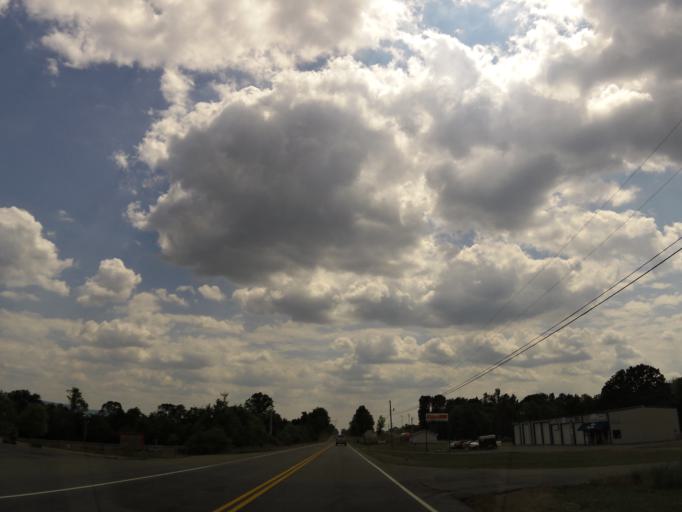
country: US
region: Tennessee
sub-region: Sequatchie County
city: Dunlap
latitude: 35.4397
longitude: -85.3472
